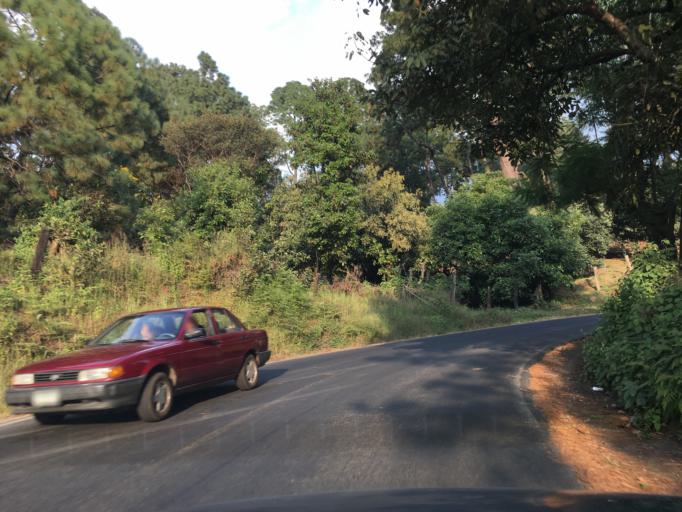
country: MX
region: Michoacan
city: Tingambato
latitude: 19.4541
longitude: -101.8912
